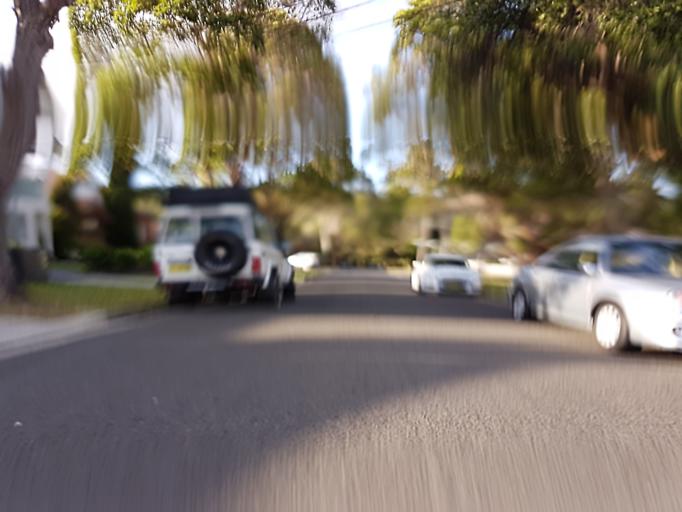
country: AU
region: New South Wales
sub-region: Manly Vale
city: Balgowlah
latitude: -33.7880
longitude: 151.2433
